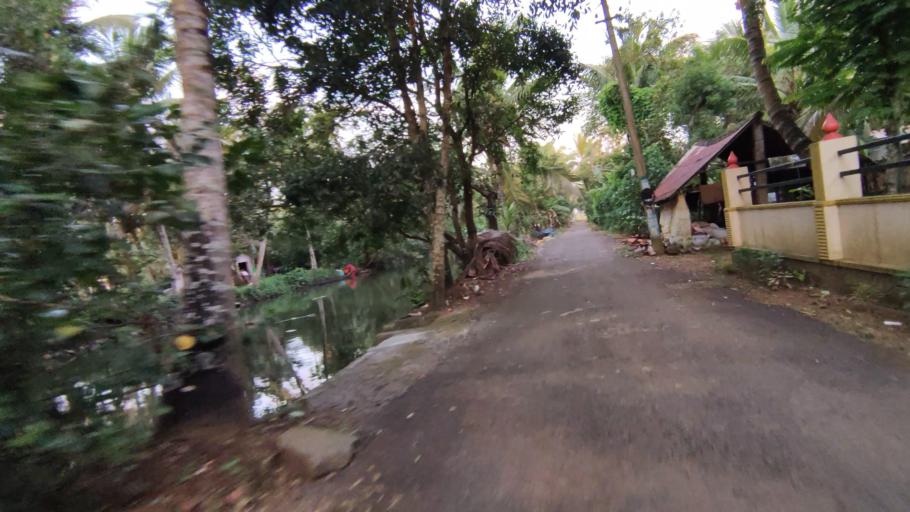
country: IN
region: Kerala
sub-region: Kottayam
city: Kottayam
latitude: 9.5759
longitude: 76.4556
